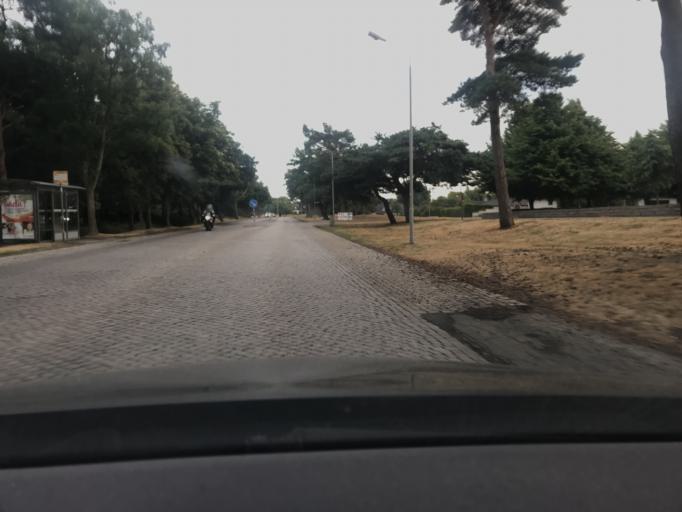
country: SE
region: Skane
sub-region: Simrishamns Kommun
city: Simrishamn
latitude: 55.5658
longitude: 14.3358
